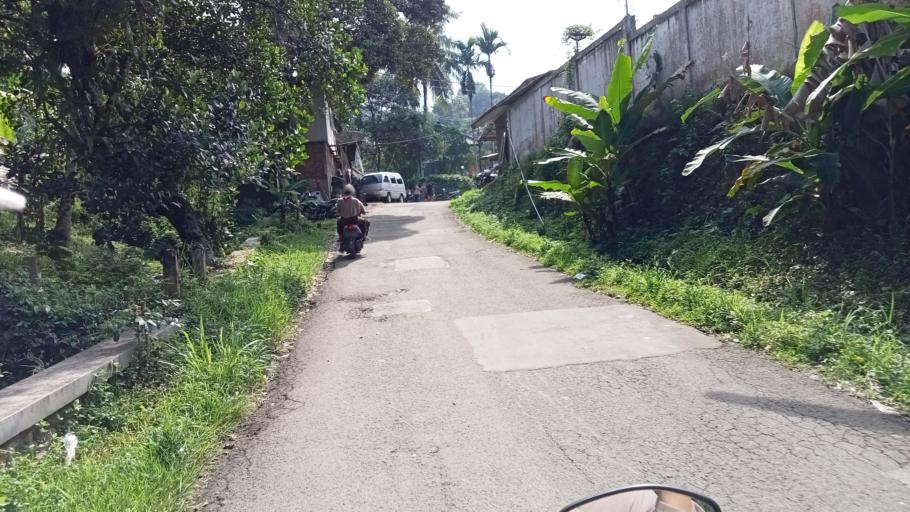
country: ID
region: West Java
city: Caringin
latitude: -6.6454
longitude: 106.9099
